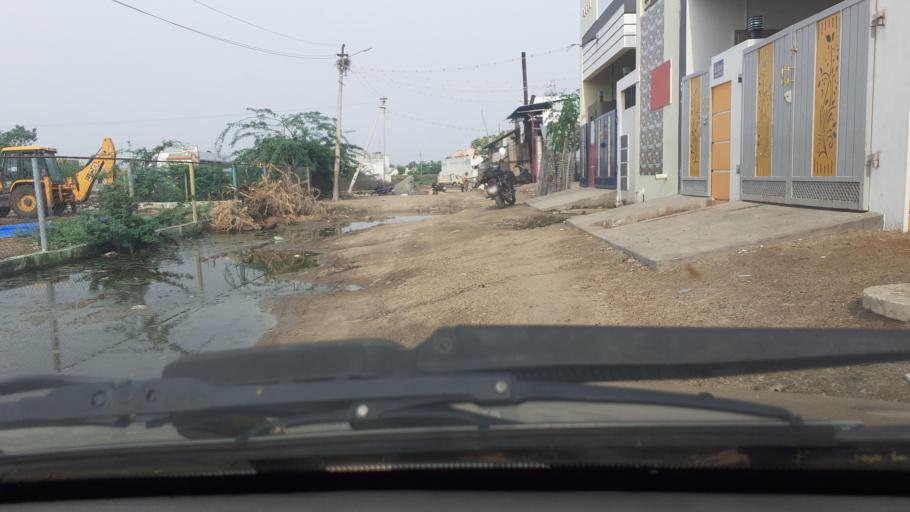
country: IN
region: Tamil Nadu
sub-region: Thoothukkudi
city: Korampallam
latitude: 8.7971
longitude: 78.1061
